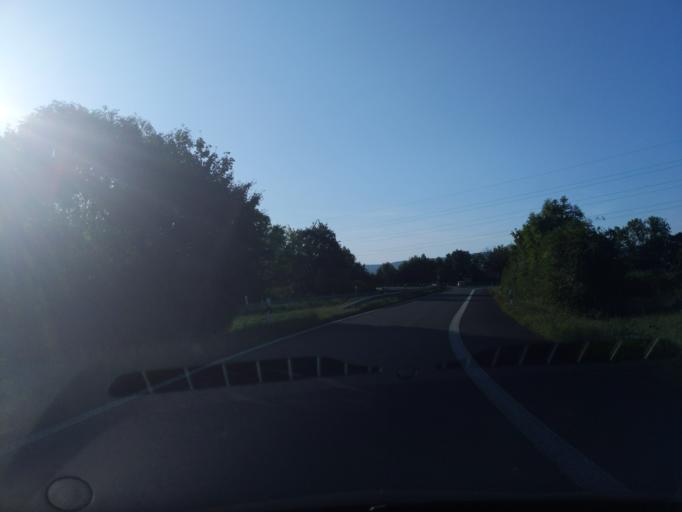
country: DE
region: Rheinland-Pfalz
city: Nieder-Ingelheim
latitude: 49.9961
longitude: 8.0929
